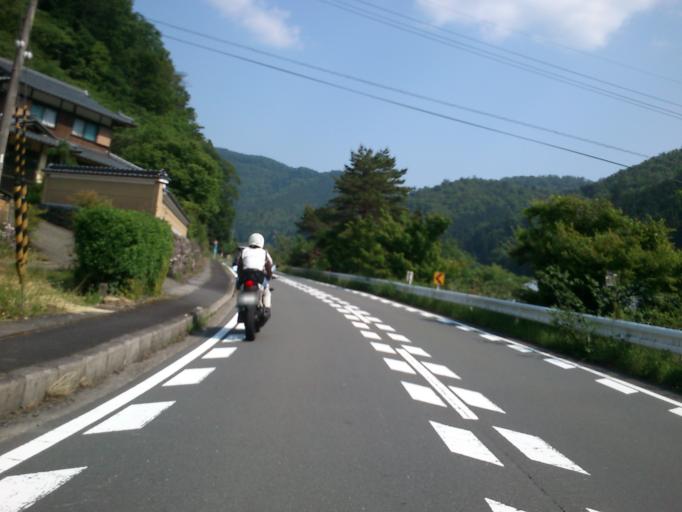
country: JP
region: Kyoto
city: Kameoka
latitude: 35.2364
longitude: 135.5643
